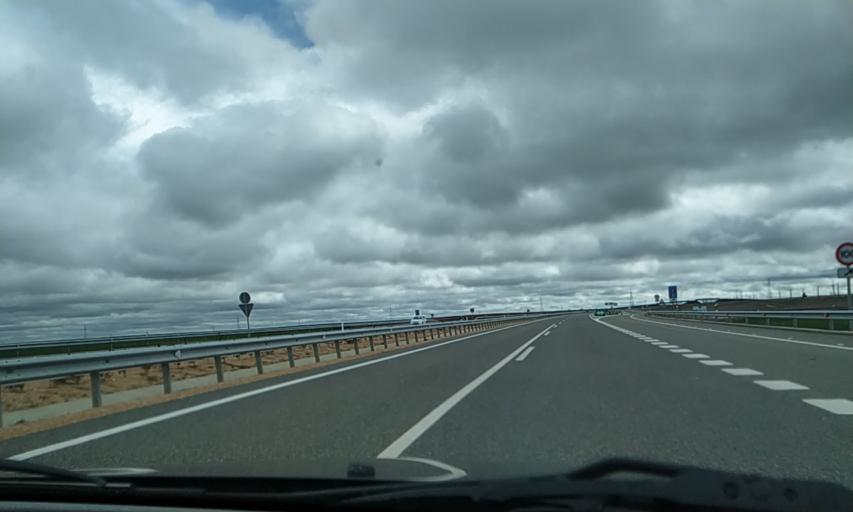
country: ES
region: Castille and Leon
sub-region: Provincia de Zamora
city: Montamarta
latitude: 41.6367
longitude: -5.7907
